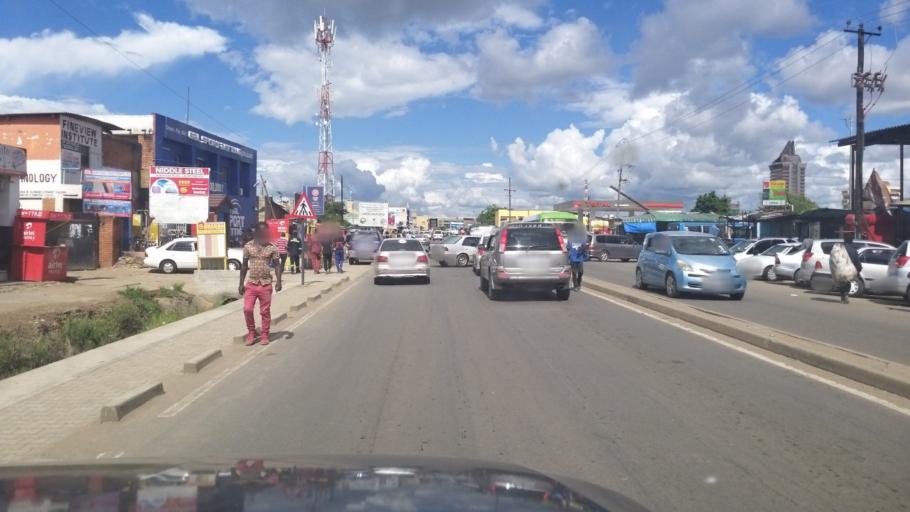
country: ZM
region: Lusaka
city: Lusaka
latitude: -15.4158
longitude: 28.2750
